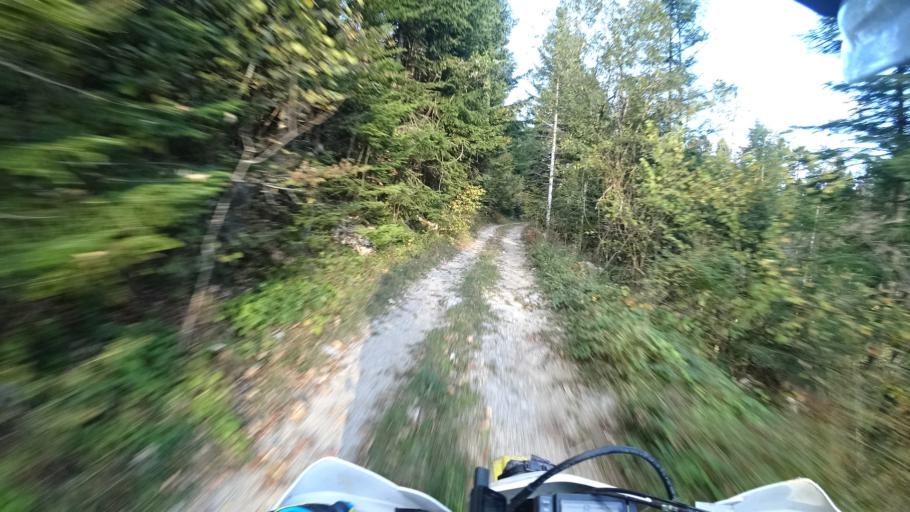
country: HR
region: Karlovacka
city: Plaski
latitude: 45.0131
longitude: 15.4348
